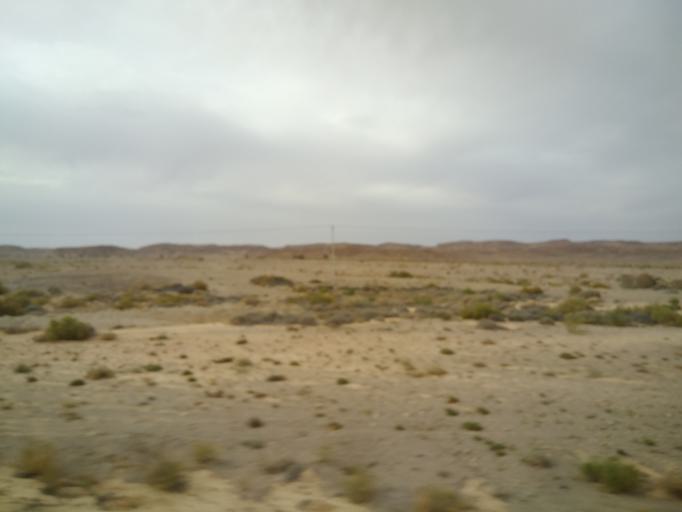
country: IL
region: Southern District
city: Eilat
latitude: 29.9273
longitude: 34.8983
